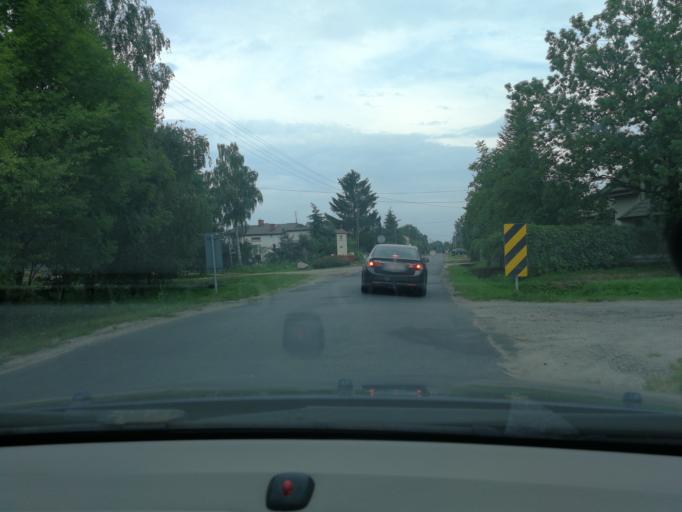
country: PL
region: Masovian Voivodeship
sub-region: Powiat grodziski
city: Grodzisk Mazowiecki
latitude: 52.1298
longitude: 20.6006
